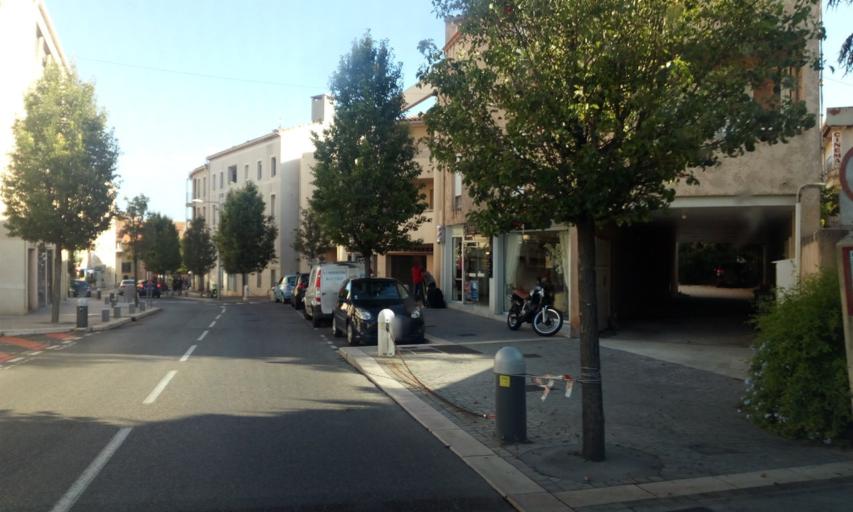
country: FR
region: Provence-Alpes-Cote d'Azur
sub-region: Departement du Var
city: Bandol
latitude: 43.1369
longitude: 5.7524
